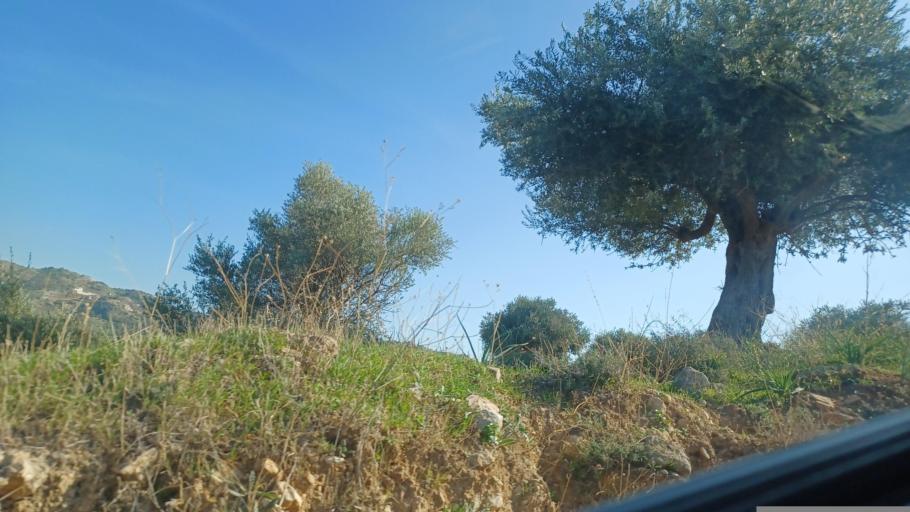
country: CY
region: Pafos
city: Mesogi
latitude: 34.7644
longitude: 32.5758
